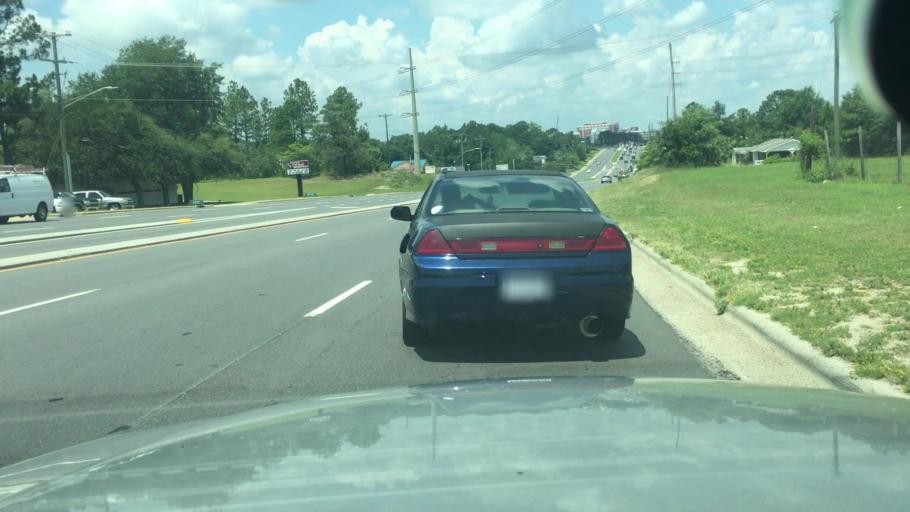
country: US
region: North Carolina
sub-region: Cumberland County
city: Fayetteville
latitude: 35.0225
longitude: -78.9220
